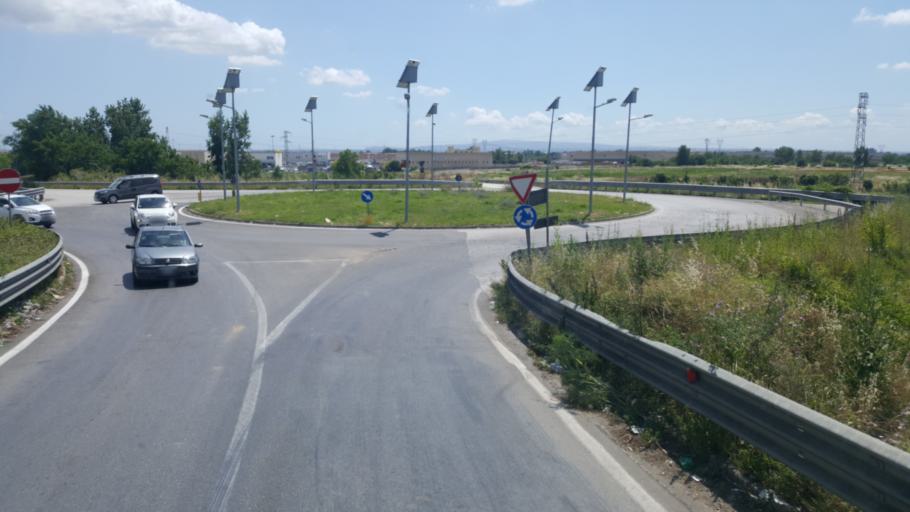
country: IT
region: Campania
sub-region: Provincia di Caserta
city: Maddaloni
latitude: 41.0145
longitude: 14.3712
